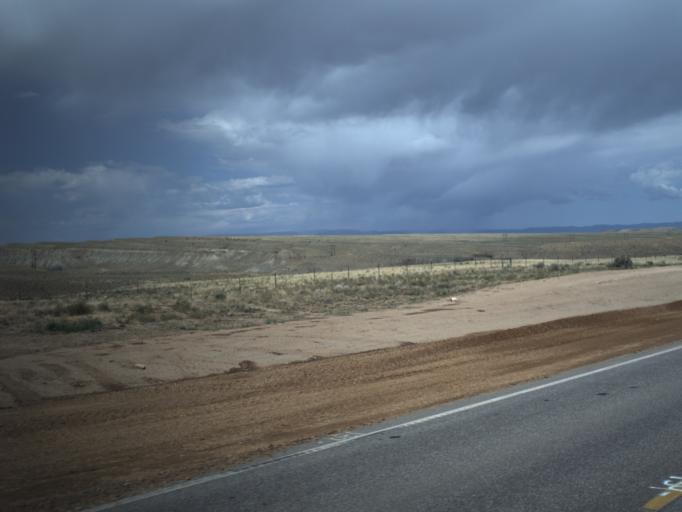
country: US
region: Utah
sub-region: Carbon County
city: East Carbon City
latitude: 39.4491
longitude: -110.4735
